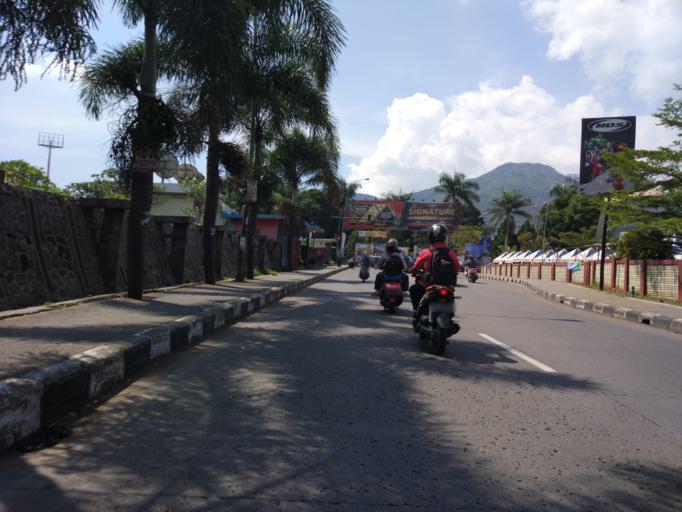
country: ID
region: West Java
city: Cileunyi
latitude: -6.9317
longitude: 107.7754
